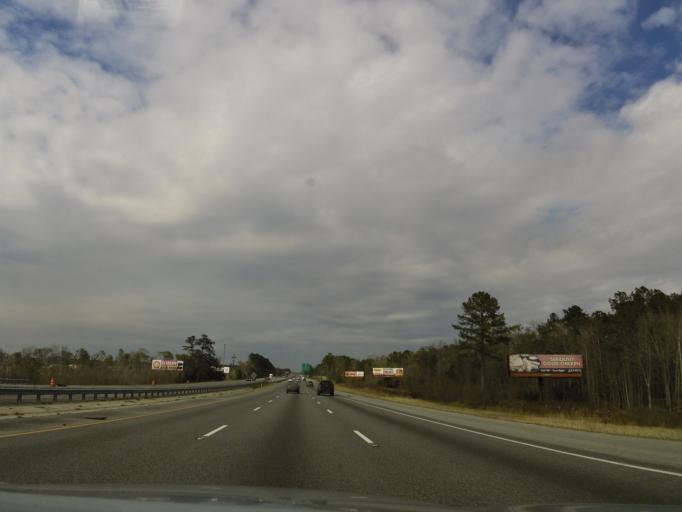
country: US
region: Georgia
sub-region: Bryan County
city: Richmond Hill
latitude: 31.9143
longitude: -81.3266
